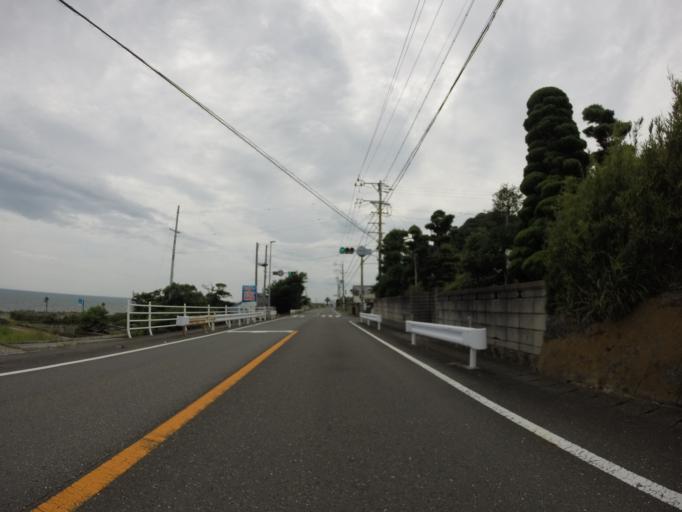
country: JP
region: Shizuoka
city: Shizuoka-shi
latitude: 34.9731
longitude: 138.4942
